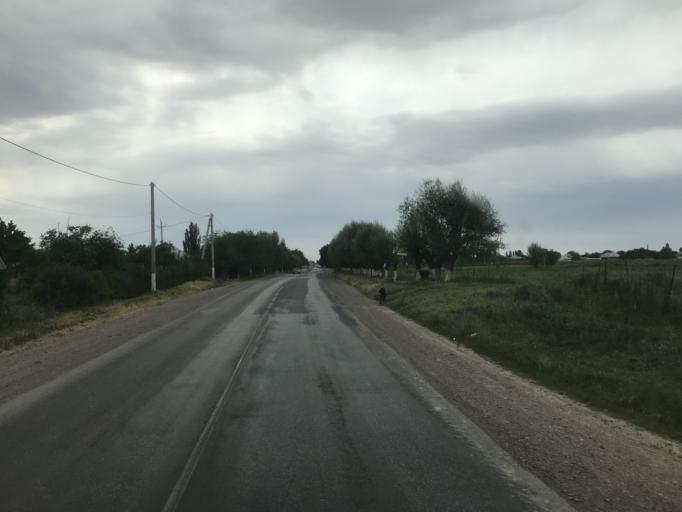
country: KZ
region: Ongtustik Qazaqstan
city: Saryaghash
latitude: 41.3760
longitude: 69.0114
